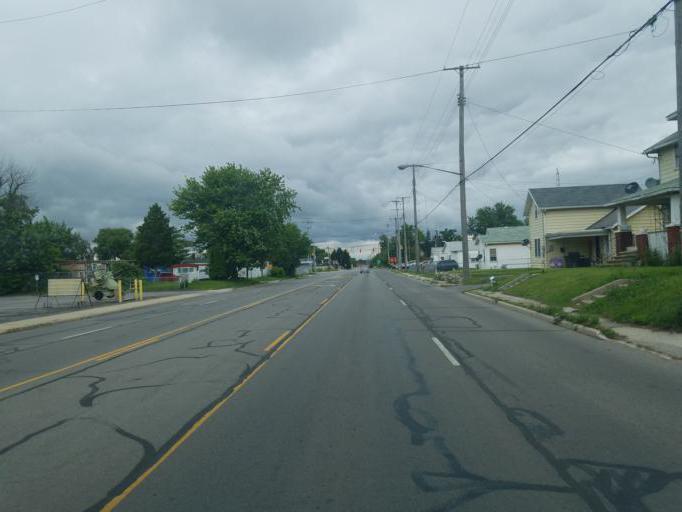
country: US
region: Ohio
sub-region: Marion County
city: Marion
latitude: 40.6064
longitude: -83.1300
